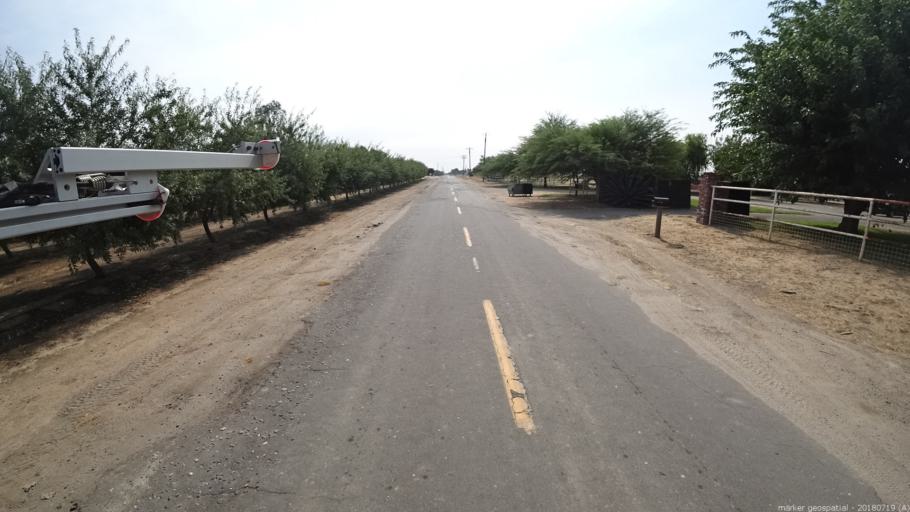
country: US
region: California
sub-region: Madera County
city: Fairmead
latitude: 37.1055
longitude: -120.2134
